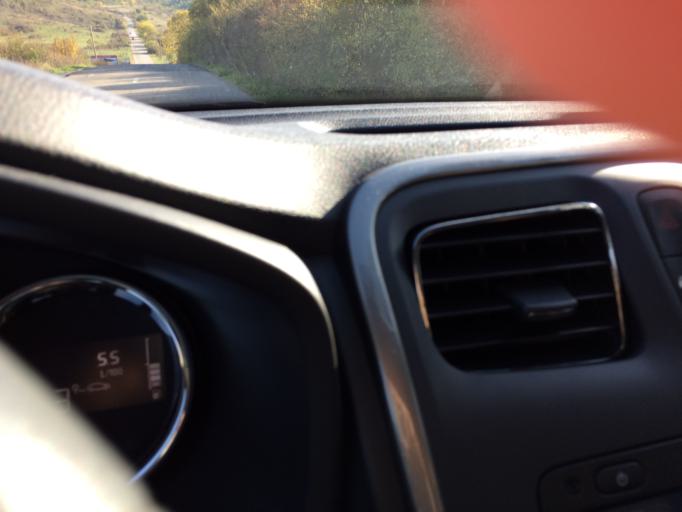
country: RO
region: Timis
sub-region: Oras Recas
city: Recas
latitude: 45.8483
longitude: 21.5190
